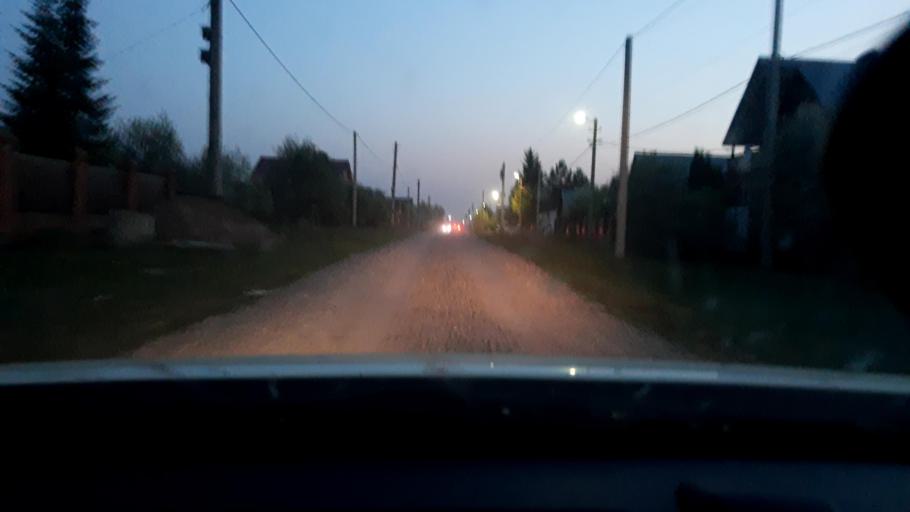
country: RU
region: Bashkortostan
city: Avdon
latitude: 54.5466
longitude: 55.7684
